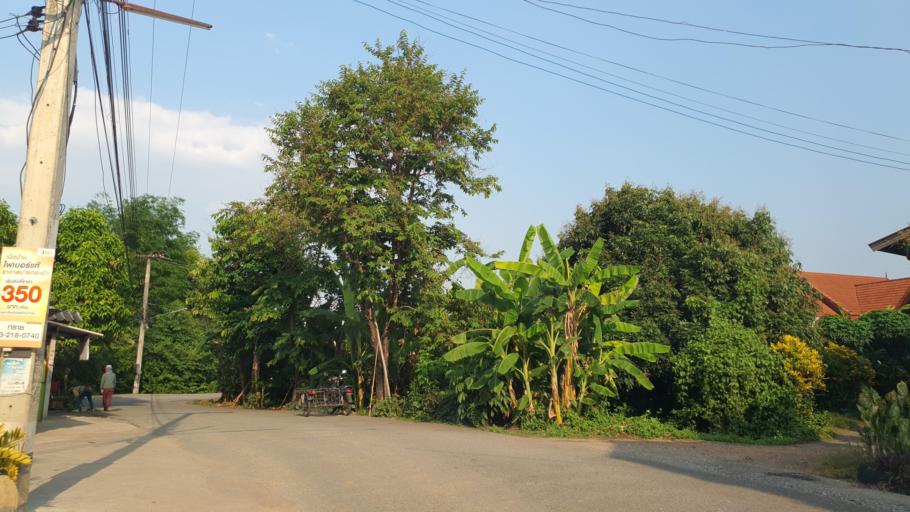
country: TH
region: Chiang Mai
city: Mae Wang
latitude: 18.6731
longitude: 98.8128
